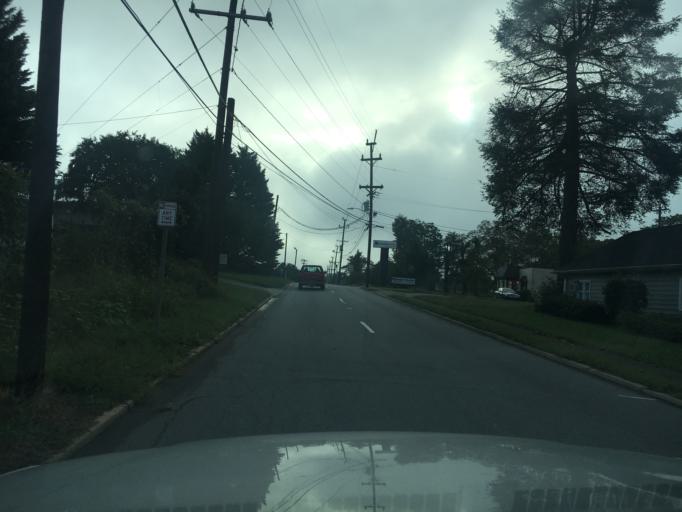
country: US
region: North Carolina
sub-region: Catawba County
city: Hickory
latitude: 35.7300
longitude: -81.3474
